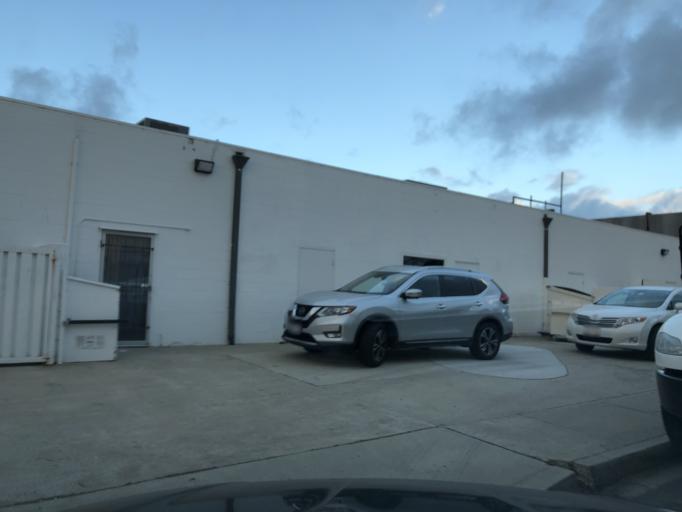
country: US
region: California
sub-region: San Diego County
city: La Jolla
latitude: 32.8331
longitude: -117.1733
